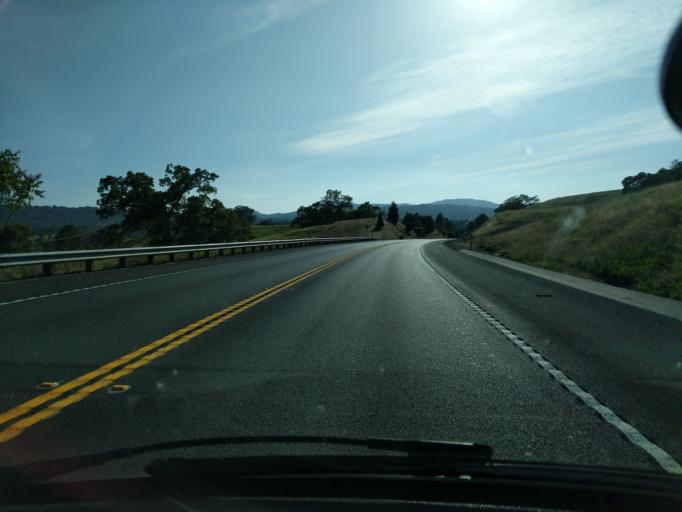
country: US
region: California
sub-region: Calaveras County
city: Angels Camp
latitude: 38.0717
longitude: -120.5813
